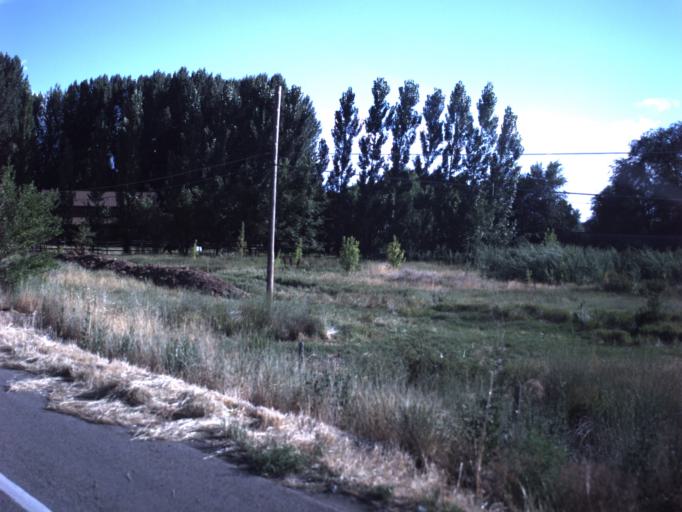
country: US
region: Utah
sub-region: Utah County
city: Springville
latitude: 40.1481
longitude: -111.6041
